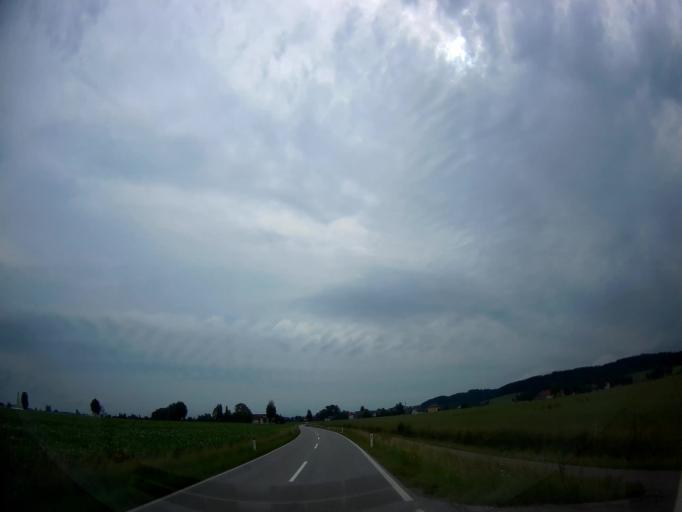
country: AT
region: Upper Austria
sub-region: Politischer Bezirk Braunau am Inn
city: Altheim
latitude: 48.2612
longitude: 13.2565
